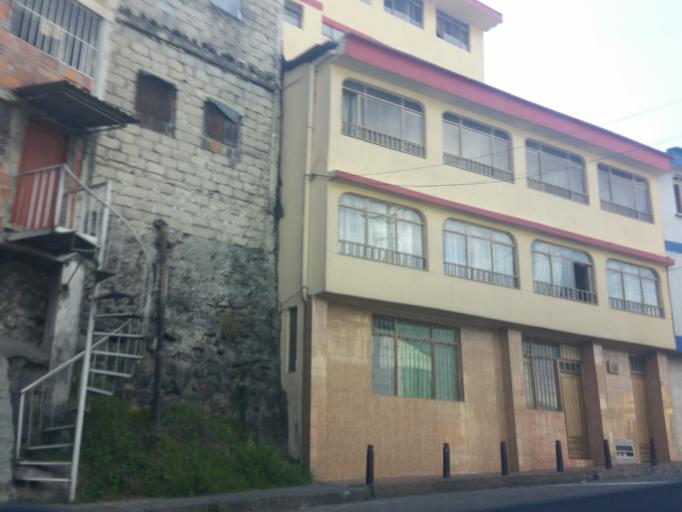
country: CO
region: Caldas
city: Manizales
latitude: 5.0687
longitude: -75.4942
